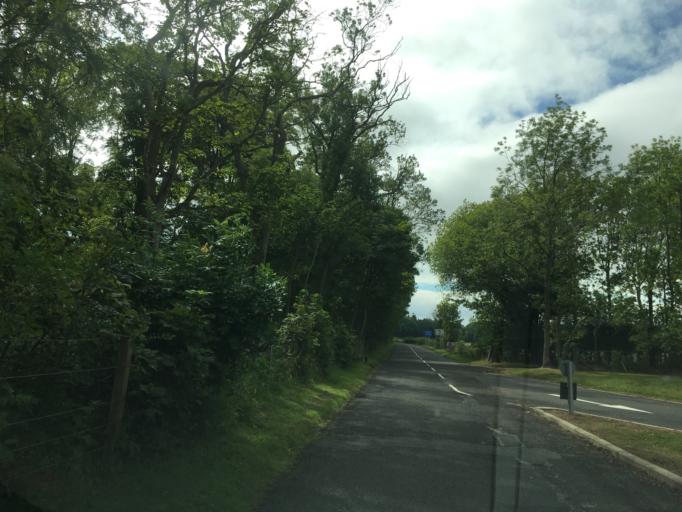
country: GB
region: Scotland
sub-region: East Lothian
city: North Berwick
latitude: 55.9940
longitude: -2.7240
